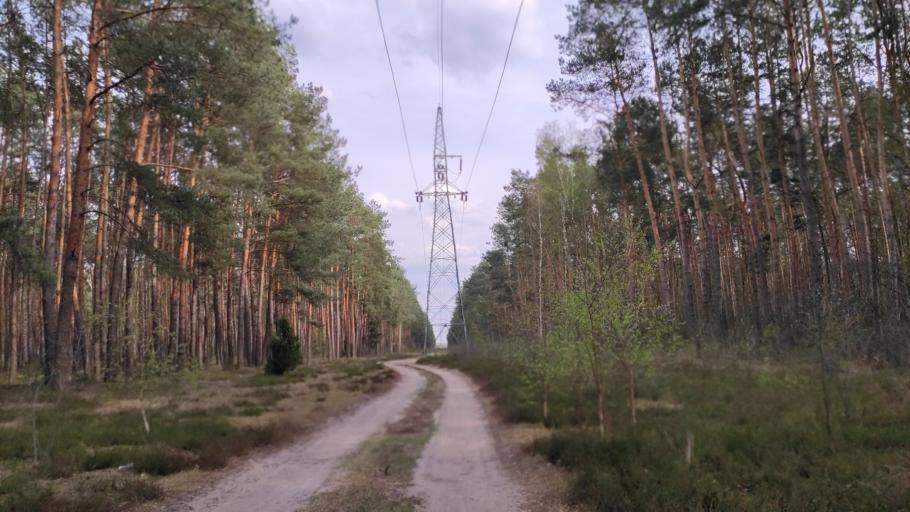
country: PL
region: Masovian Voivodeship
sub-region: Powiat grojecki
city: Warka
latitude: 51.7531
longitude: 21.1867
